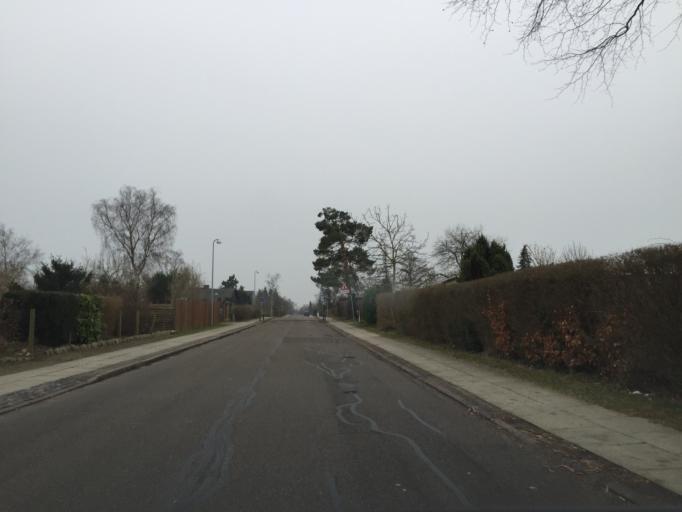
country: DK
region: Capital Region
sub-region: Fureso Kommune
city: Farum
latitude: 55.8138
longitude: 12.3623
